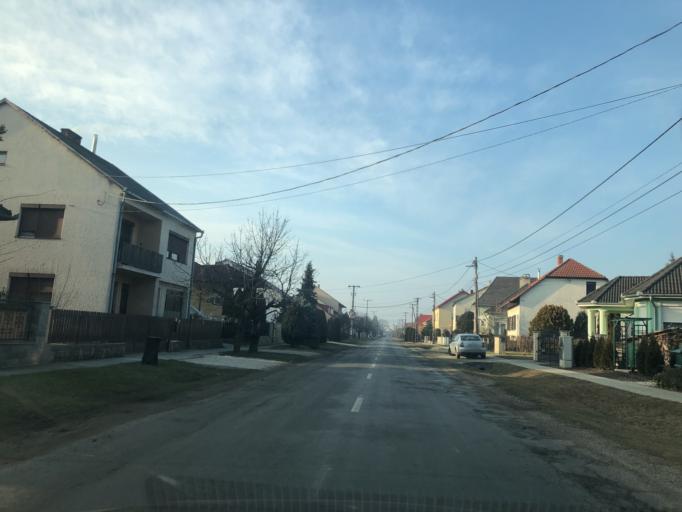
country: HU
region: Gyor-Moson-Sopron
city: Kapuvar
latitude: 47.5905
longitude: 17.0958
